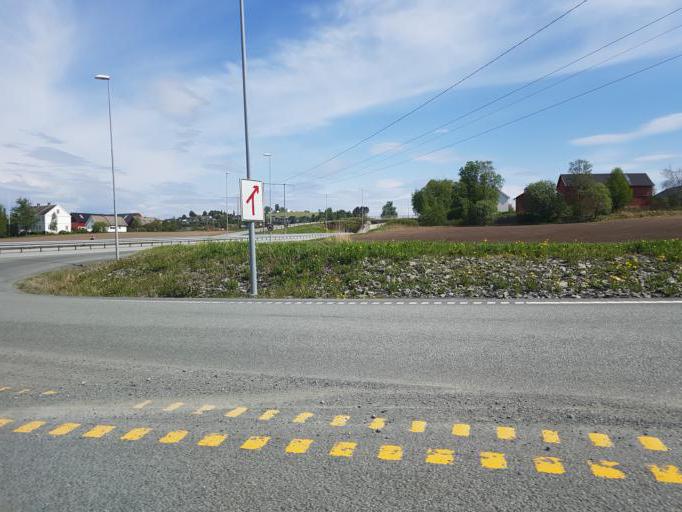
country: NO
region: Nord-Trondelag
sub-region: Levanger
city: Levanger
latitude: 63.7315
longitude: 11.2929
